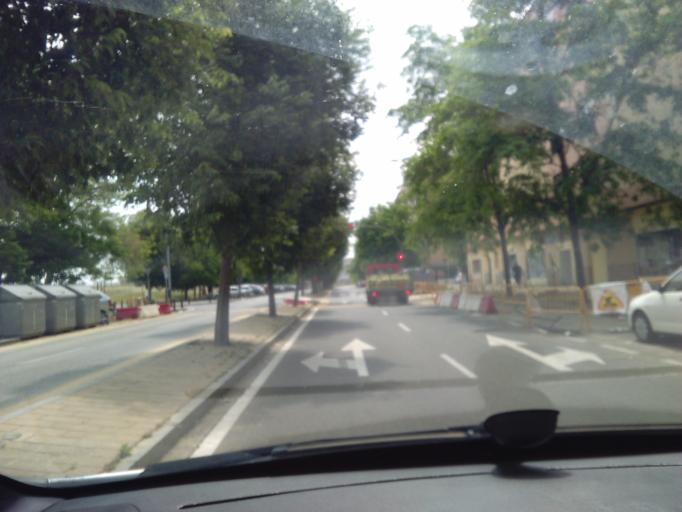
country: ES
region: Andalusia
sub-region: Provincia de Sevilla
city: Sevilla
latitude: 37.3669
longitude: -5.9525
